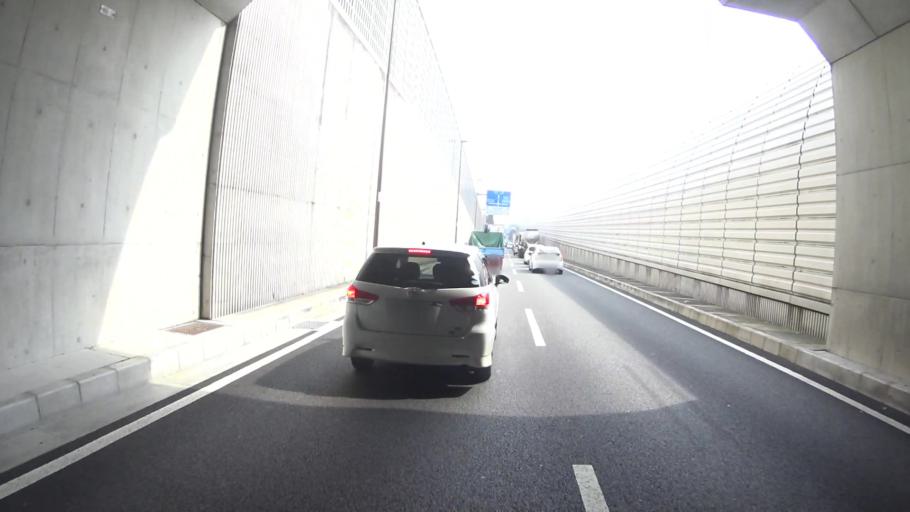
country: JP
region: Kyoto
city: Tanabe
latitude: 34.8113
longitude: 135.7137
